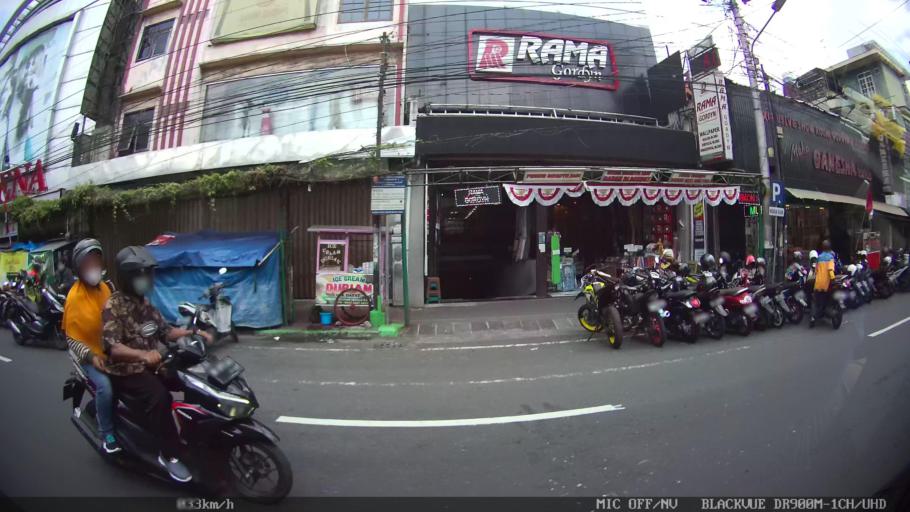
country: ID
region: Daerah Istimewa Yogyakarta
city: Yogyakarta
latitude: -7.7832
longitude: 110.3814
